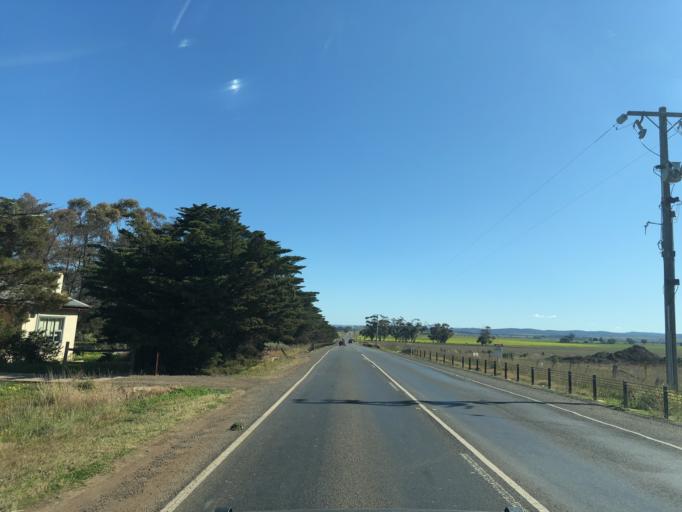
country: AU
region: Victoria
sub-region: Hume
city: Diggers Rest
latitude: -37.6284
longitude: 144.6999
